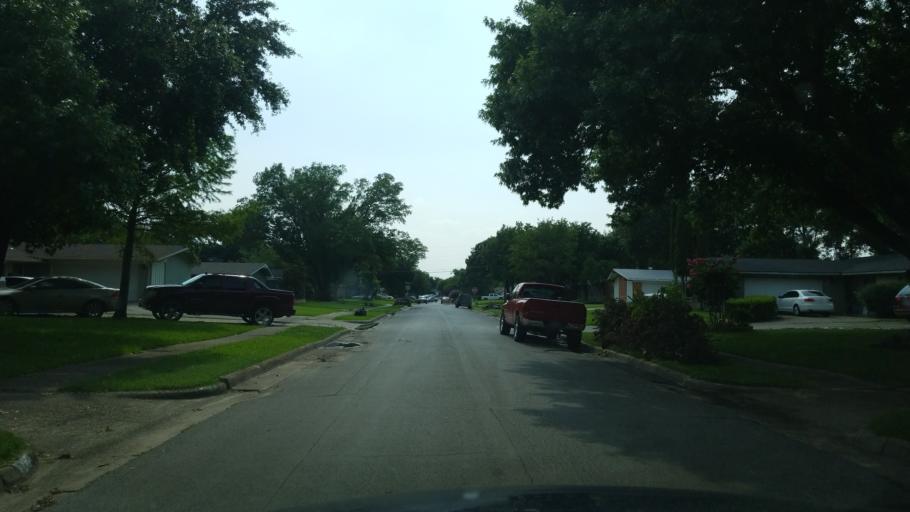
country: US
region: Texas
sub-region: Dallas County
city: Farmers Branch
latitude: 32.9022
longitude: -96.8769
